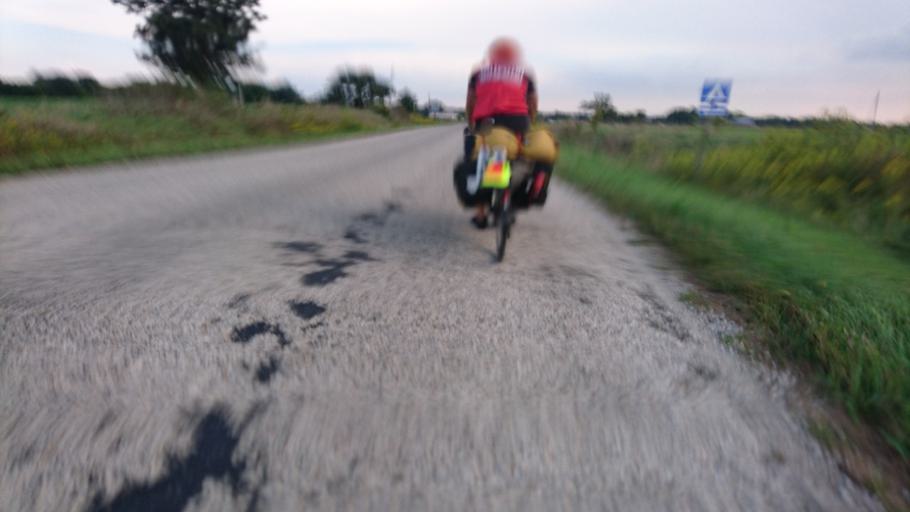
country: US
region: Illinois
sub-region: Logan County
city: Atlanta
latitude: 40.2246
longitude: -89.1990
